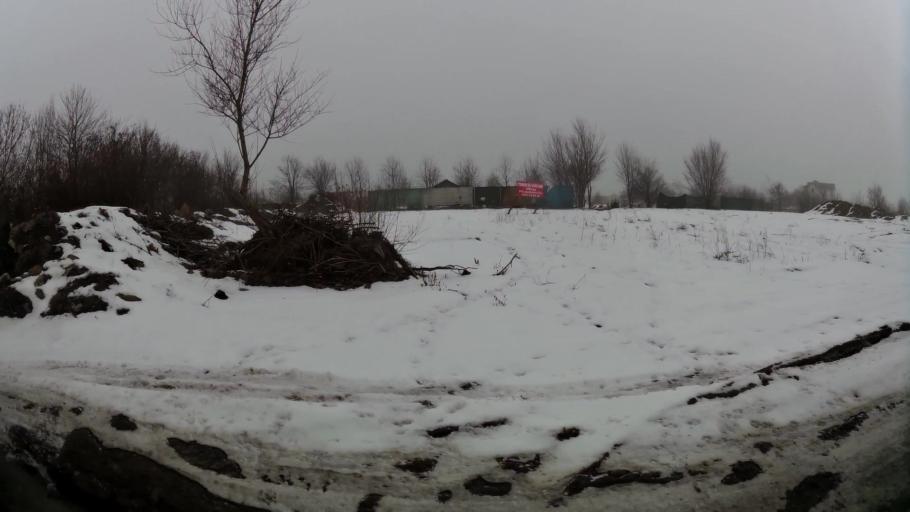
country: RO
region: Ilfov
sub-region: Comuna Chiajna
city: Rosu
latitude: 44.4477
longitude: 26.0264
